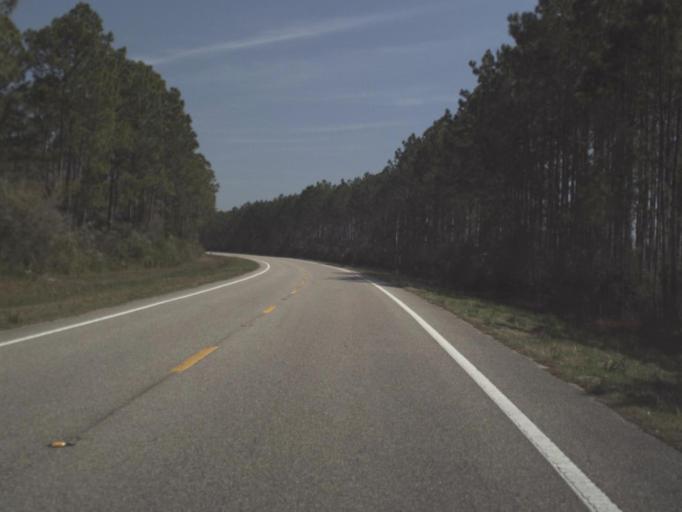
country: US
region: Florida
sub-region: Gulf County
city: Port Saint Joe
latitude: 29.7421
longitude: -85.2284
